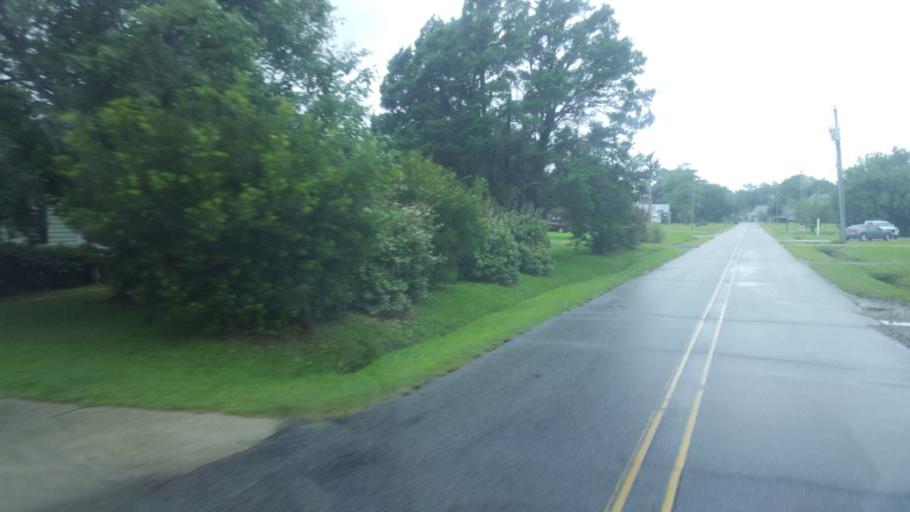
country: US
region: North Carolina
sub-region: Dare County
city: Wanchese
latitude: 35.8412
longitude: -75.6252
